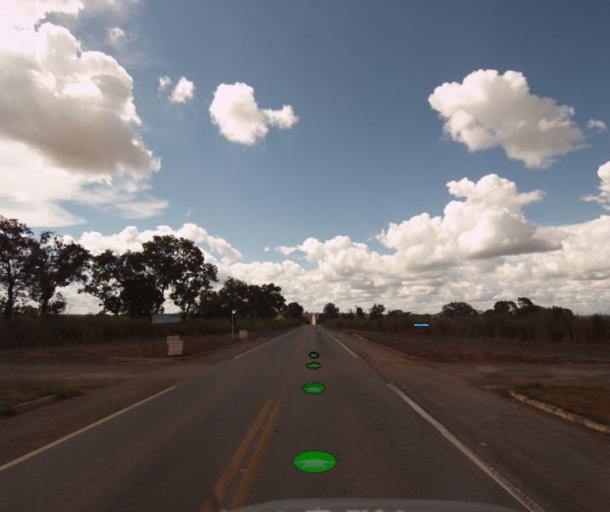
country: BR
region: Goias
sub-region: Porangatu
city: Porangatu
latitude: -13.4825
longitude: -49.1363
